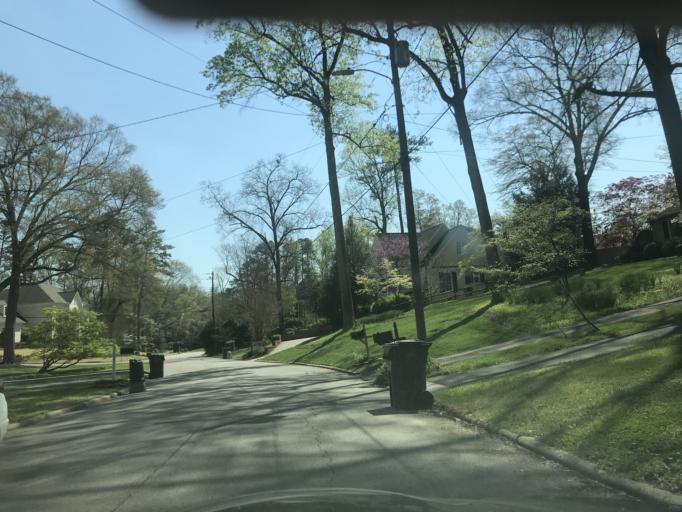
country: US
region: North Carolina
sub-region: Wake County
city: West Raleigh
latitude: 35.8249
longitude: -78.6421
